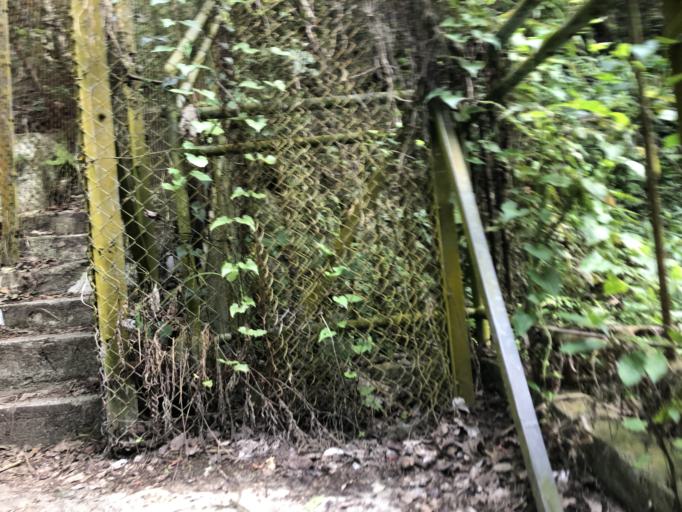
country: HK
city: Hong Kong
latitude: 22.2803
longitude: 114.1202
